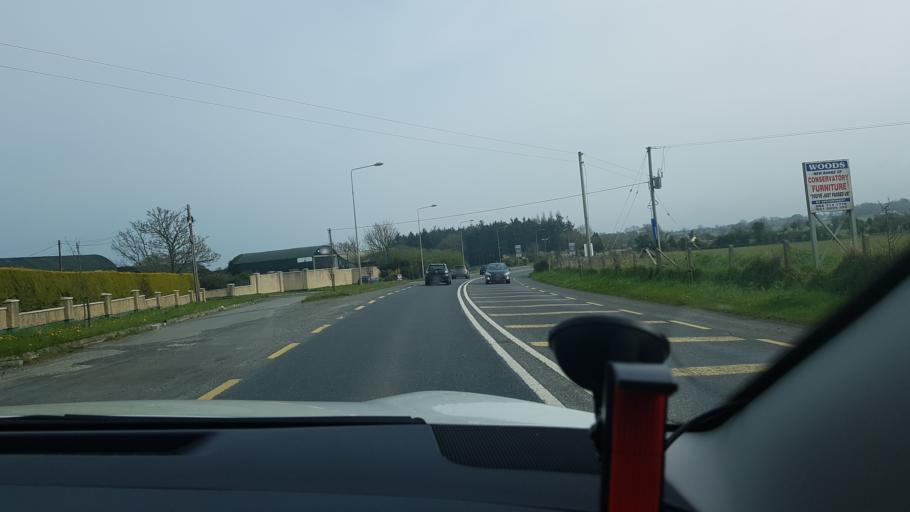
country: IE
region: Leinster
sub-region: An Mhi
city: Stamullin
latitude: 53.6651
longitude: -6.2736
